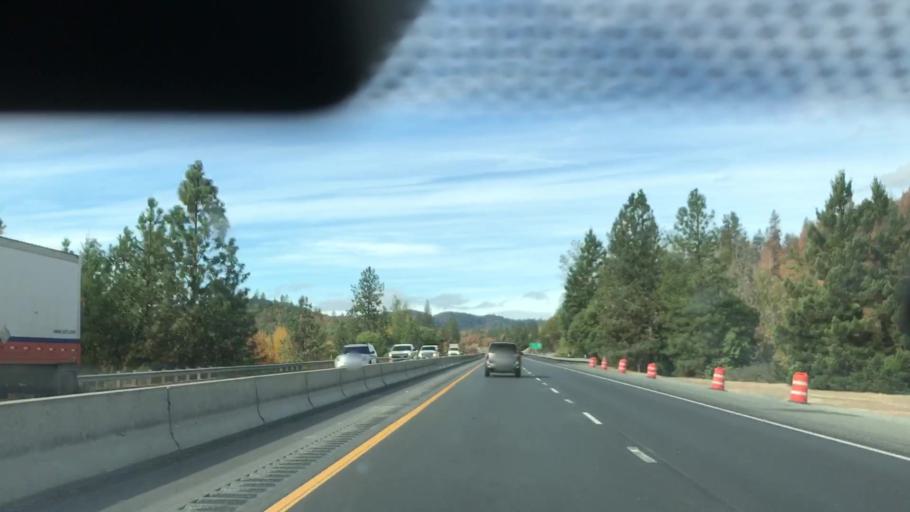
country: US
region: Oregon
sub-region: Josephine County
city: Fruitdale
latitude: 42.4313
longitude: -123.2543
